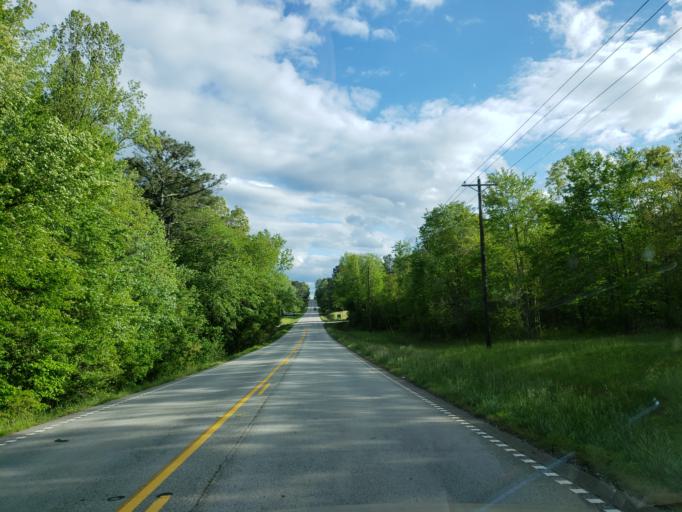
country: US
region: Georgia
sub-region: Haralson County
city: Tallapoosa
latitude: 33.8189
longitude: -85.2920
